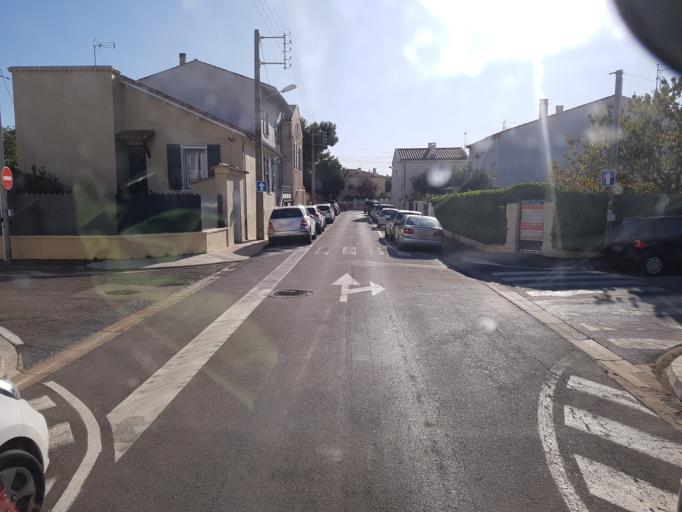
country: FR
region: Languedoc-Roussillon
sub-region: Departement de l'Aude
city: Narbonne
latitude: 43.1787
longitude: 3.0058
